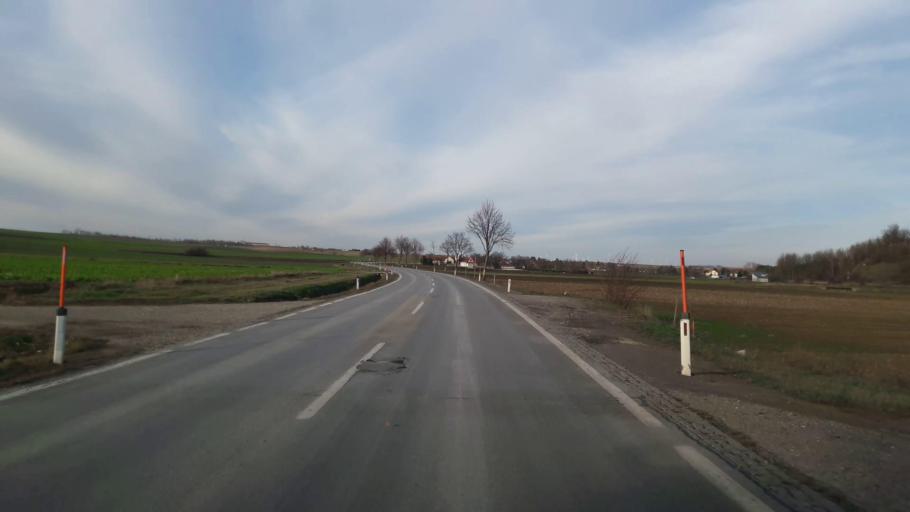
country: AT
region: Lower Austria
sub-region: Politischer Bezirk Ganserndorf
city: Bad Pirawarth
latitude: 48.4331
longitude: 16.6094
